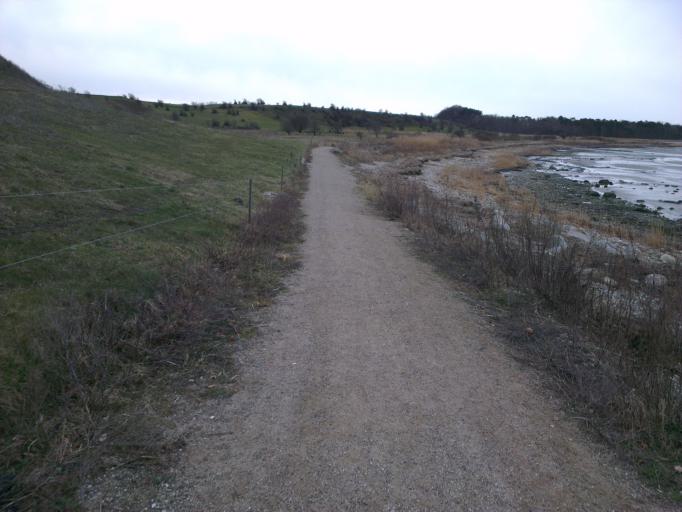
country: DK
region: Capital Region
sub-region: Frederikssund Kommune
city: Skibby
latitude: 55.8057
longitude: 11.8807
